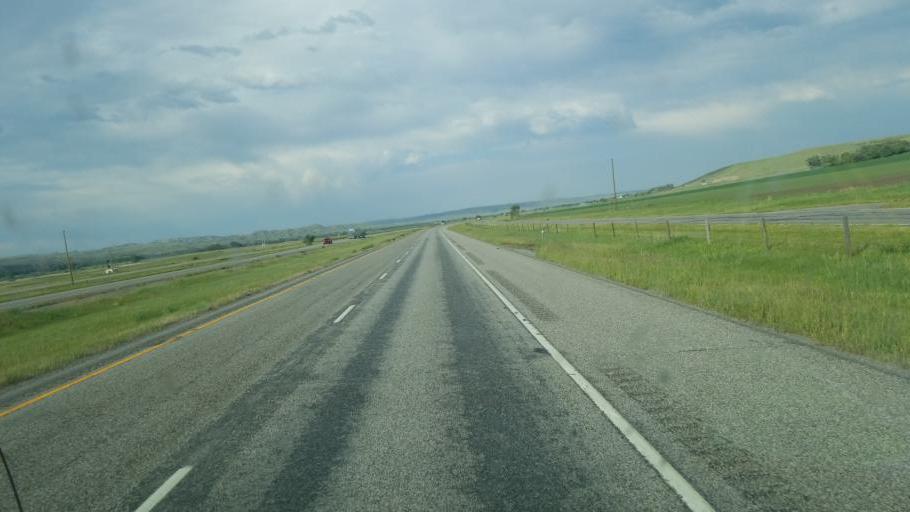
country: US
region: Montana
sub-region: Sweet Grass County
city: Big Timber
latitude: 45.8026
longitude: -110.0232
